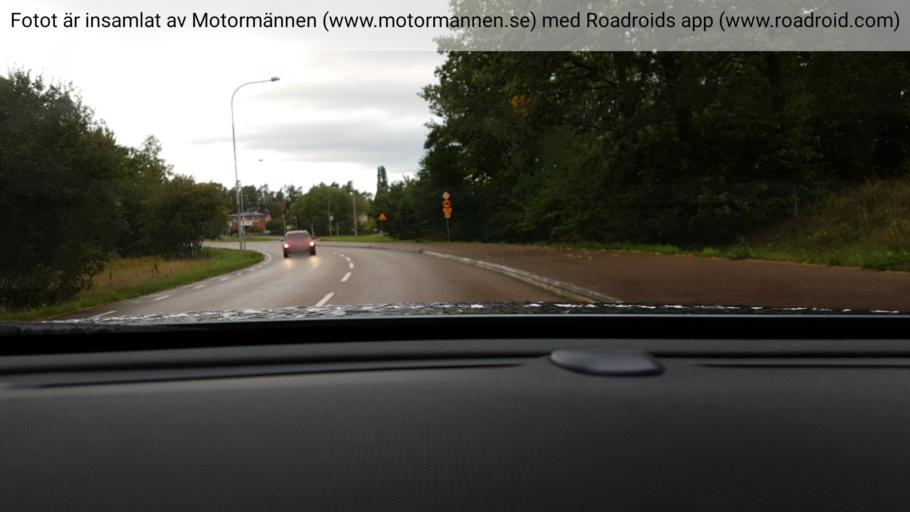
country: SE
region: Vaestra Goetaland
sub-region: Vanersborgs Kommun
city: Vargon
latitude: 58.3454
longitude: 12.3543
